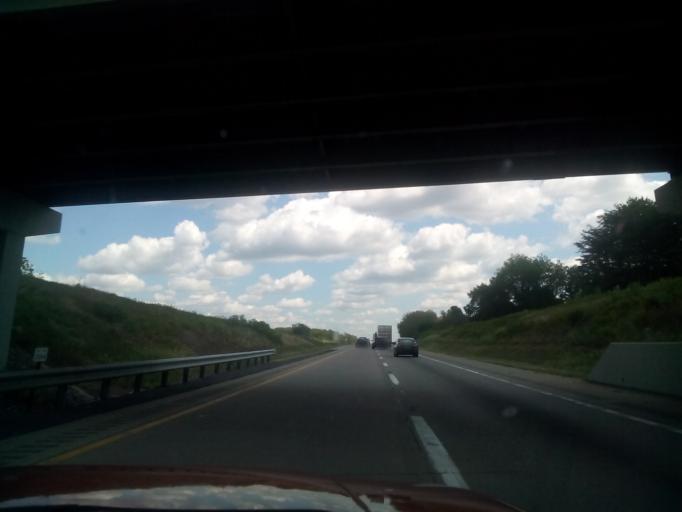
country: US
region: Pennsylvania
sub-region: Northumberland County
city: Riverside
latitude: 40.9867
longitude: -76.7069
